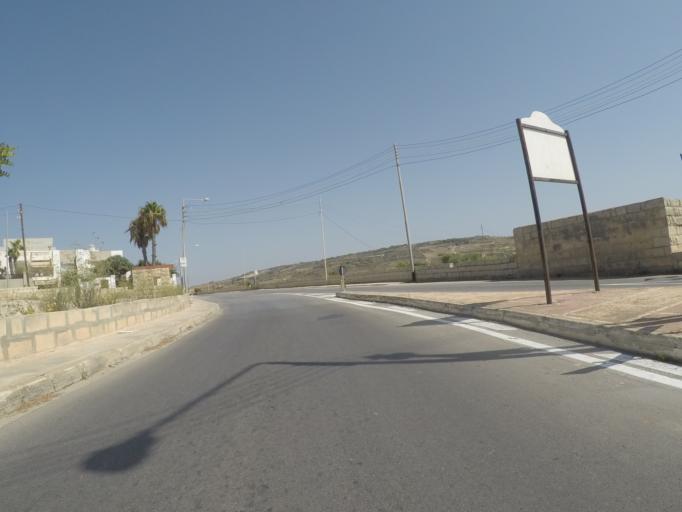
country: MT
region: L-Imgarr
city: Imgarr
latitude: 35.9191
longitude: 14.3727
